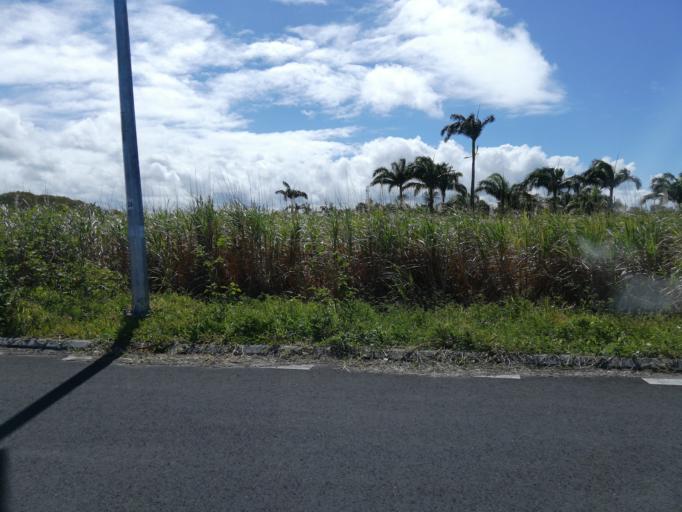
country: MU
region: Grand Port
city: Beau Vallon
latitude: -20.4504
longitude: 57.6936
